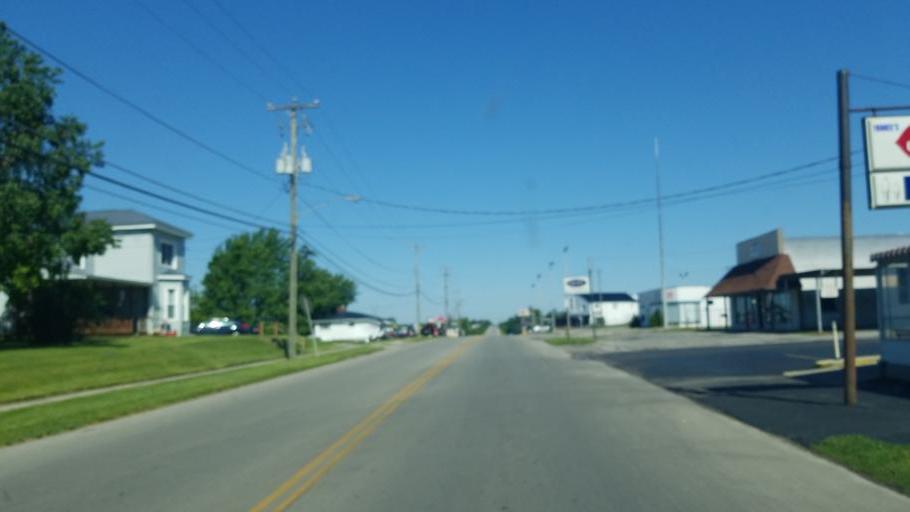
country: US
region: Ohio
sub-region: Hardin County
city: Kenton
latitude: 40.6504
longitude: -83.6215
